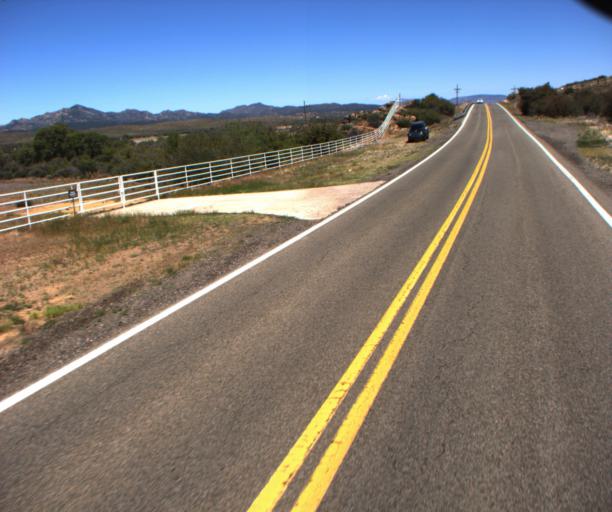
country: US
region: Arizona
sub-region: Yavapai County
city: Congress
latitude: 34.2421
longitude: -112.7366
